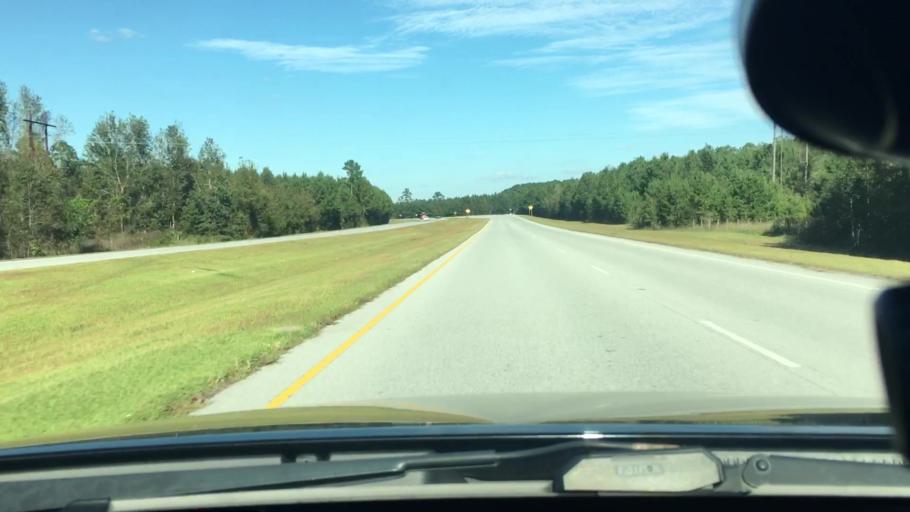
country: US
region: North Carolina
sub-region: Craven County
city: Trent Woods
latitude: 35.1384
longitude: -77.1137
